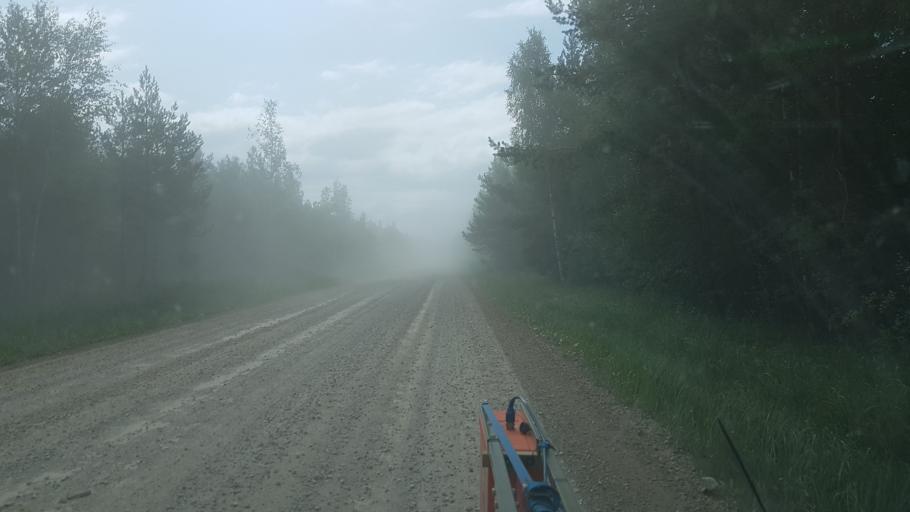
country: EE
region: Paernumaa
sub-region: Audru vald
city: Audru
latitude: 58.5309
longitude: 24.4057
